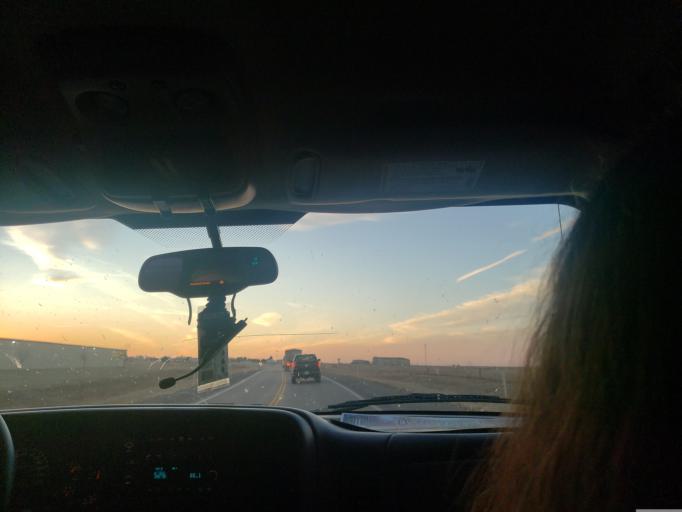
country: US
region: Kansas
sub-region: Seward County
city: Liberal
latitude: 37.0704
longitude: -100.9102
